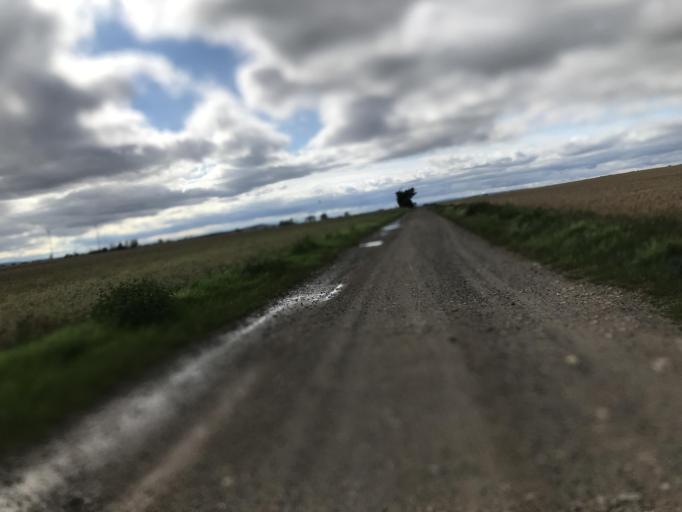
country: DE
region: Saxony-Anhalt
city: Ditfurt
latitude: 51.8104
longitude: 11.2383
